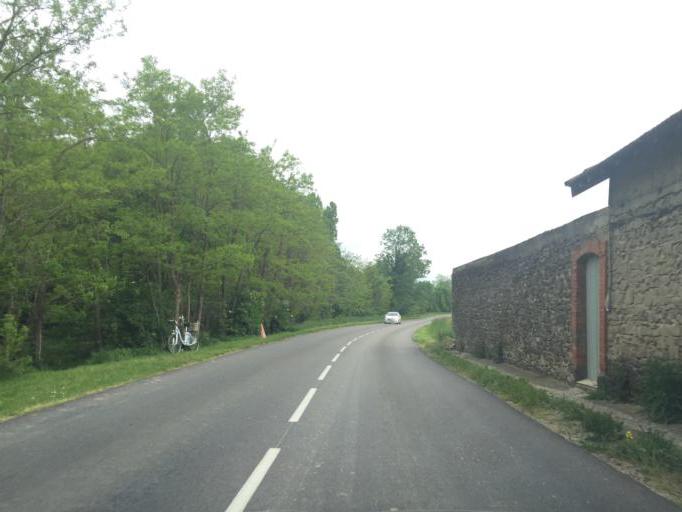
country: FR
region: Rhone-Alpes
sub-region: Departement de la Drome
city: Peyrins
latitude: 45.0765
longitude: 5.0403
